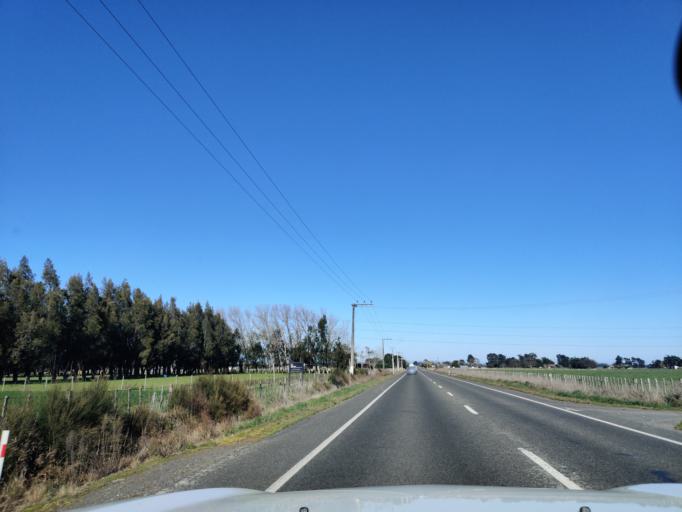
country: NZ
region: Manawatu-Wanganui
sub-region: Palmerston North City
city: Palmerston North
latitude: -40.2554
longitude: 175.5758
